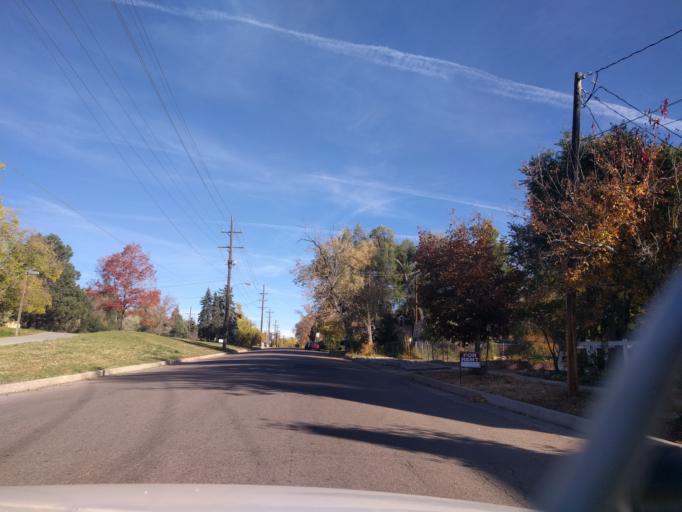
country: US
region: Colorado
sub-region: El Paso County
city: Colorado Springs
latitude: 38.8365
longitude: -104.8129
